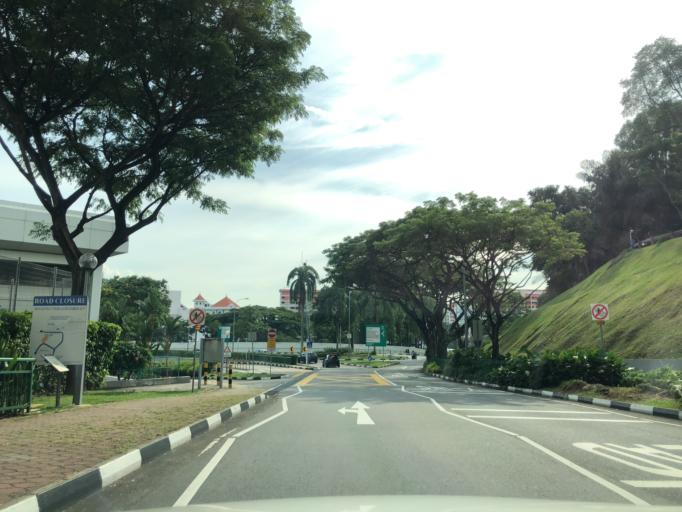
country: SG
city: Singapore
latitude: 1.2796
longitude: 103.8337
